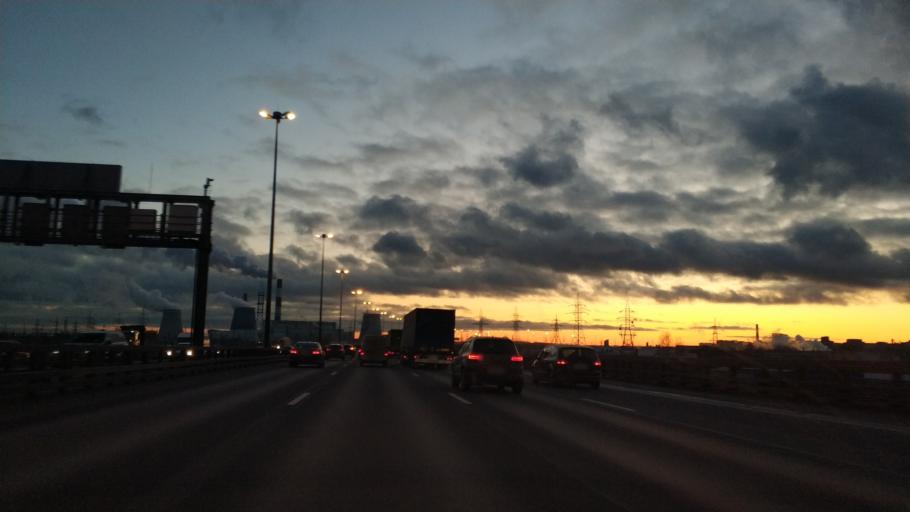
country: RU
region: St.-Petersburg
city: Obukhovo
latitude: 59.8445
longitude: 30.4571
